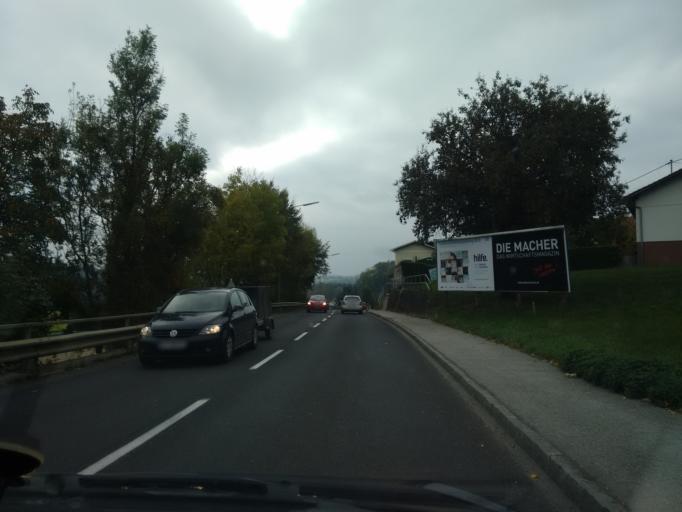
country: AT
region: Upper Austria
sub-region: Politischer Bezirk Steyr-Land
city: Bad Hall
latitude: 48.0559
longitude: 14.2001
